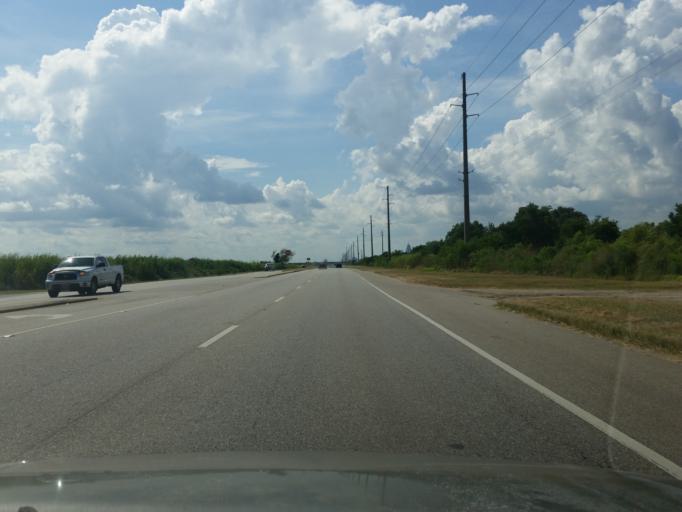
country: US
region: Alabama
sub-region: Baldwin County
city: Spanish Fort
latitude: 30.6746
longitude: -87.9649
